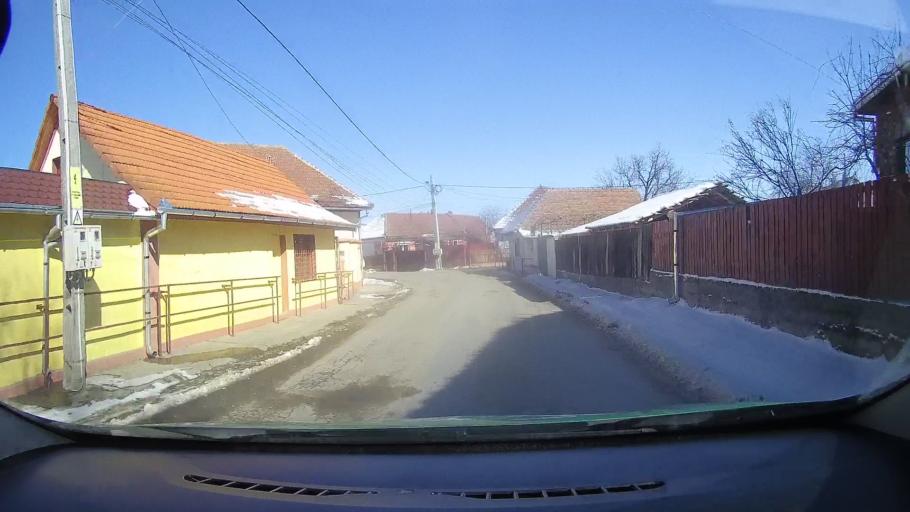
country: RO
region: Brasov
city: Ucea de Sus
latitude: 45.7500
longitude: 24.6788
